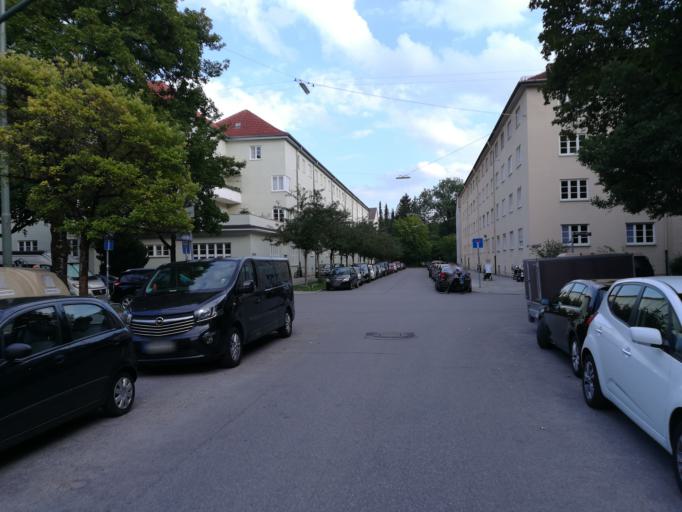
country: DE
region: Bavaria
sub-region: Upper Bavaria
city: Munich
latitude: 48.1650
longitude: 11.5333
